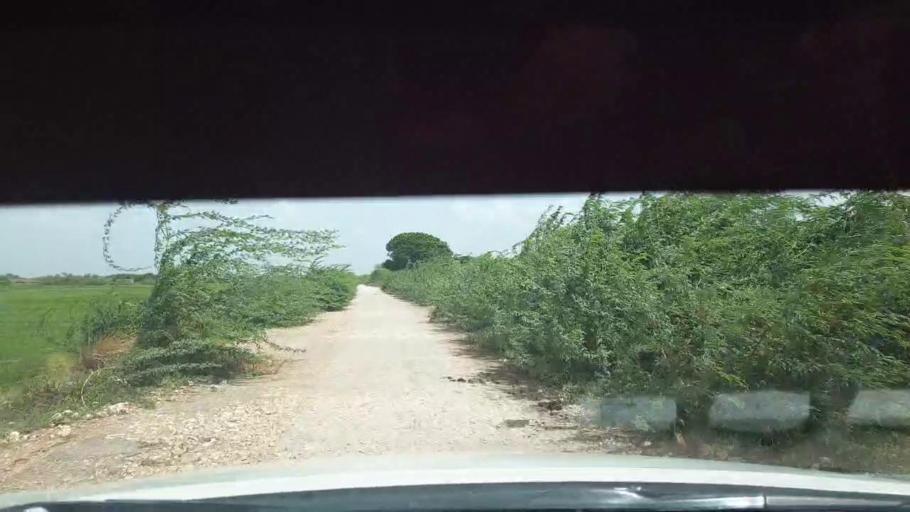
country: PK
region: Sindh
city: Kadhan
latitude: 24.5005
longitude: 68.9810
